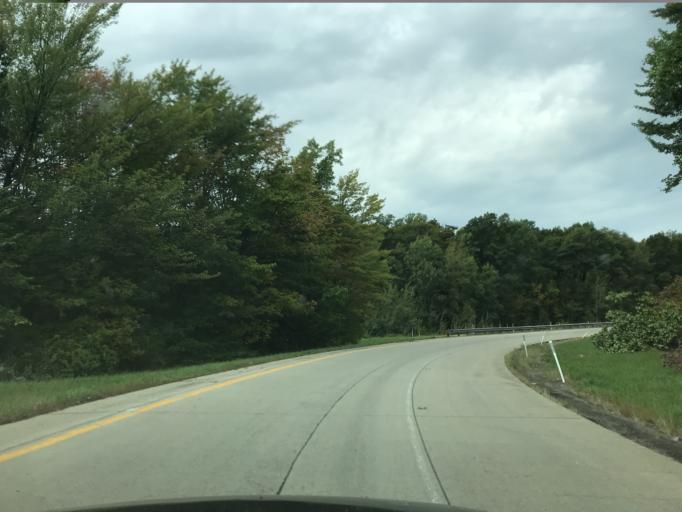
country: US
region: Pennsylvania
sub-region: Erie County
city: Erie
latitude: 42.0314
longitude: -80.1250
